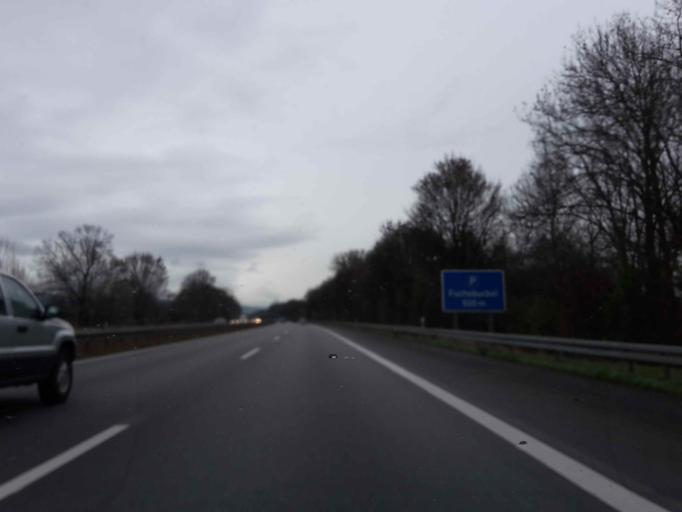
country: DE
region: Hesse
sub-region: Regierungsbezirk Darmstadt
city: Heppenheim an der Bergstrasse
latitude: 49.6287
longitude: 8.6139
